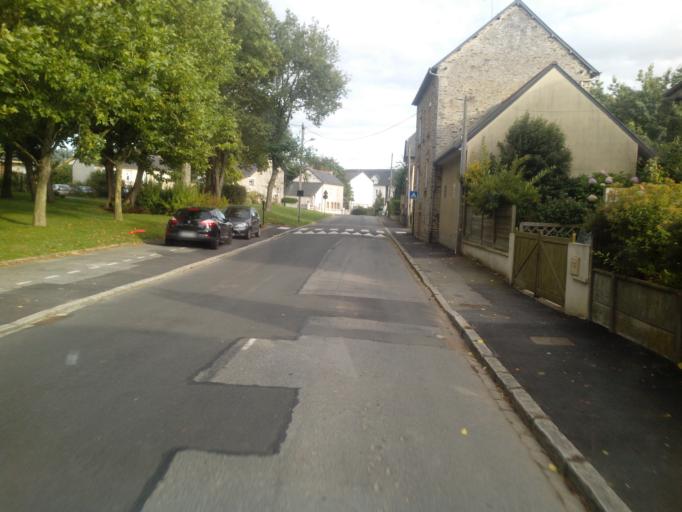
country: FR
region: Brittany
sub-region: Departement d'Ille-et-Vilaine
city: Acigne
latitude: 48.1334
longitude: -1.5390
